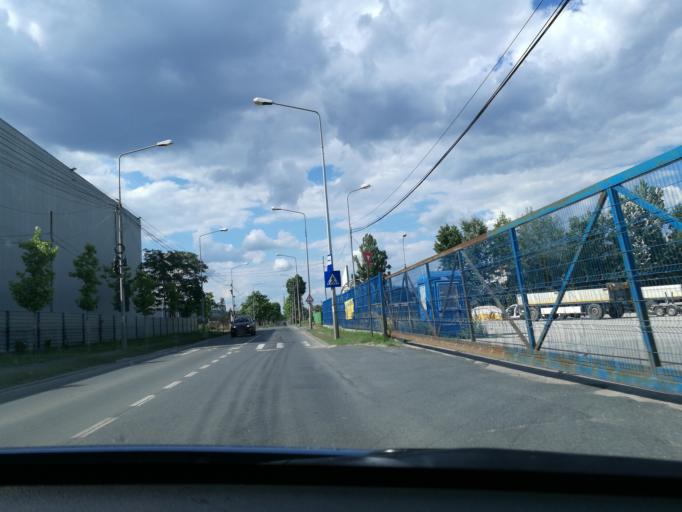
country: RO
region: Ilfov
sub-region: Comuna Glina
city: Catelu
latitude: 44.4113
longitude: 26.2183
